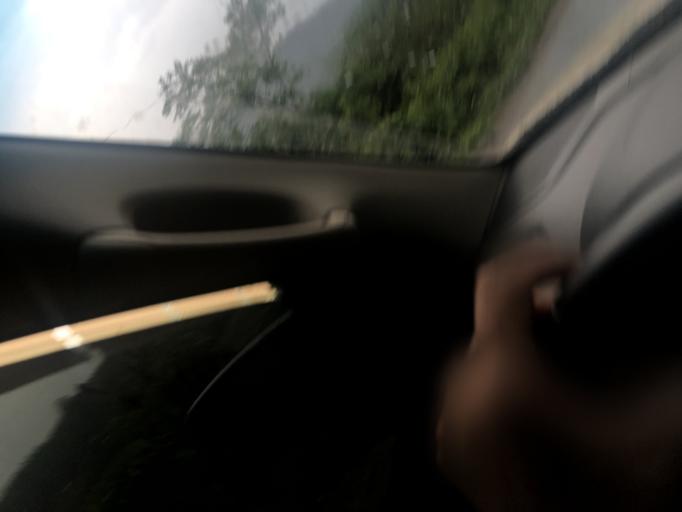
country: LA
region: Phongsali
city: Phongsali
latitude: 21.4058
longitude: 101.9614
